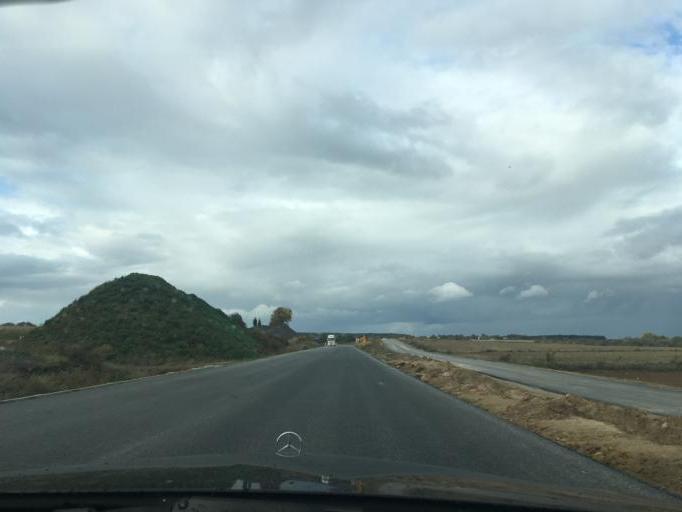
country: PL
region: Lublin Voivodeship
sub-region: Powiat lubelski
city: Krzczonow
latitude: 50.9942
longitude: 22.6787
